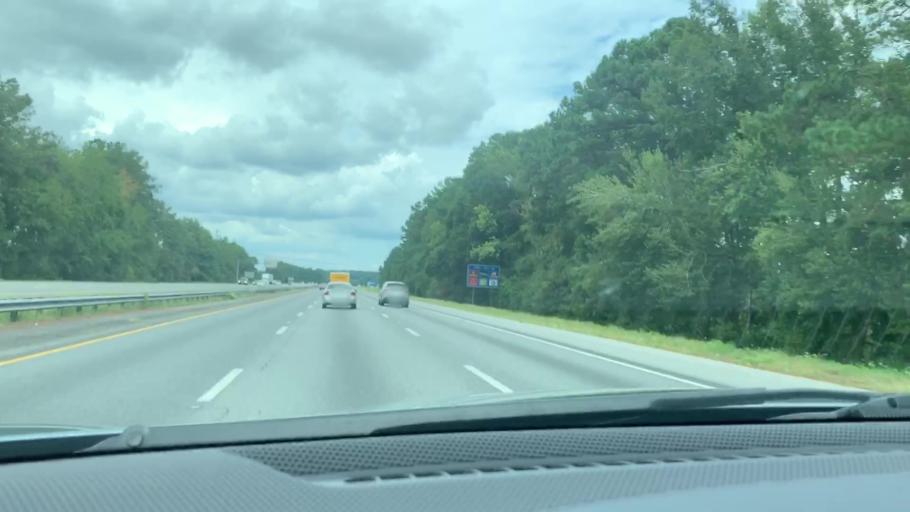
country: US
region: Georgia
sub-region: Bryan County
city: Richmond Hill
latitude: 31.9374
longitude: -81.3340
